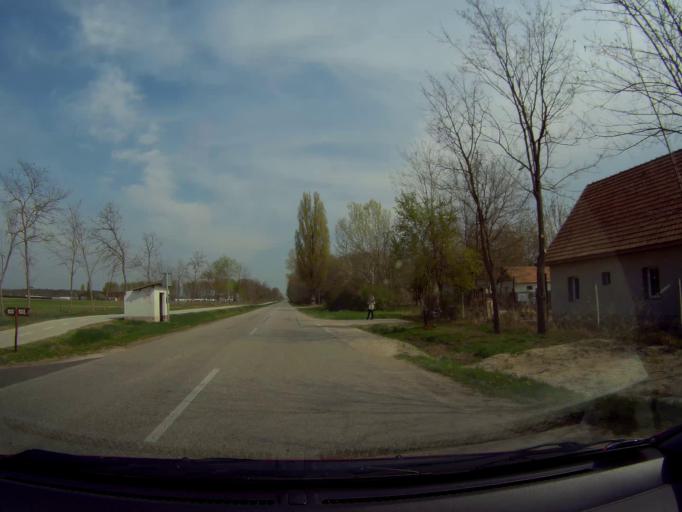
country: HU
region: Bacs-Kiskun
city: Helvecia
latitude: 46.7544
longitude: 19.6058
